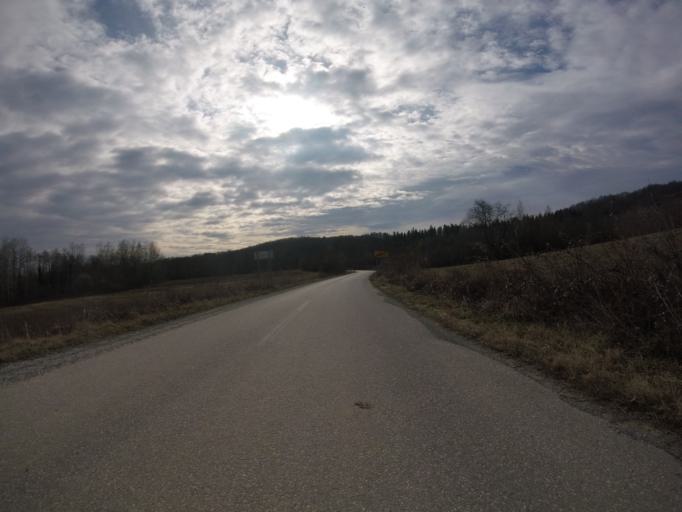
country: HR
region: Sisacko-Moslavacka
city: Glina
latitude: 45.4723
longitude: 16.0272
